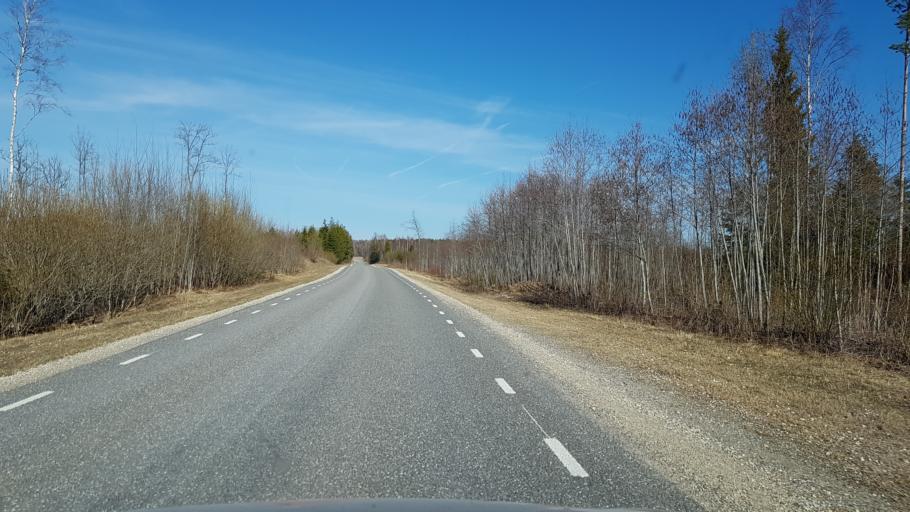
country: EE
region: Laeaene-Virumaa
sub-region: Rakke vald
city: Rakke
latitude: 59.0012
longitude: 26.3052
